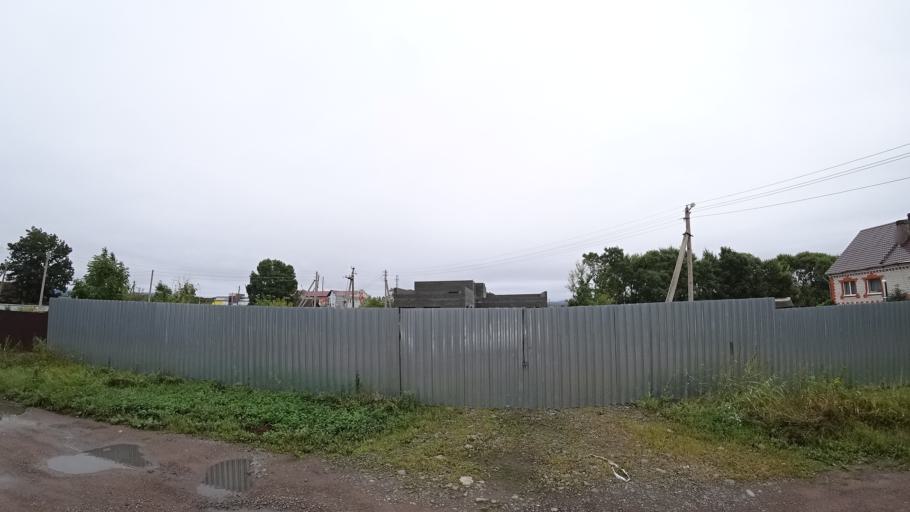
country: RU
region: Primorskiy
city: Monastyrishche
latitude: 44.2012
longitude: 132.4482
